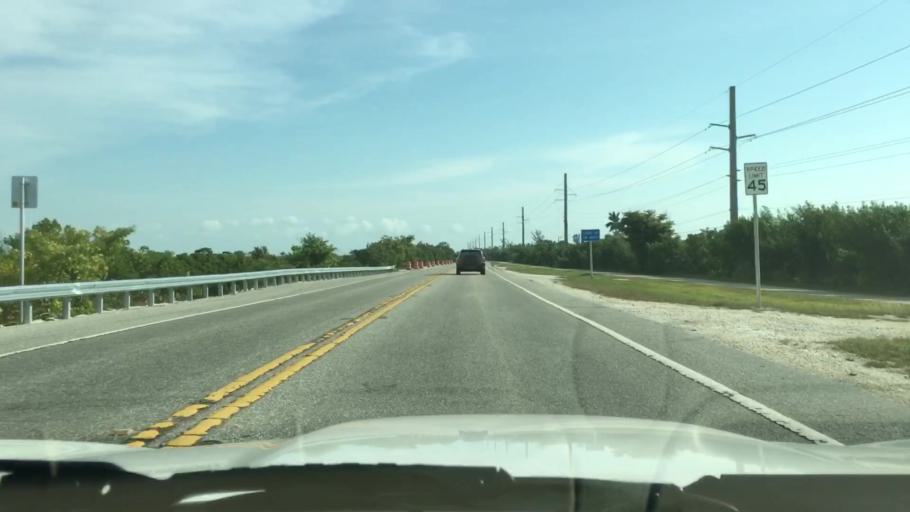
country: US
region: Florida
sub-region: Monroe County
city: Cudjoe Key
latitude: 24.6627
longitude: -81.5134
